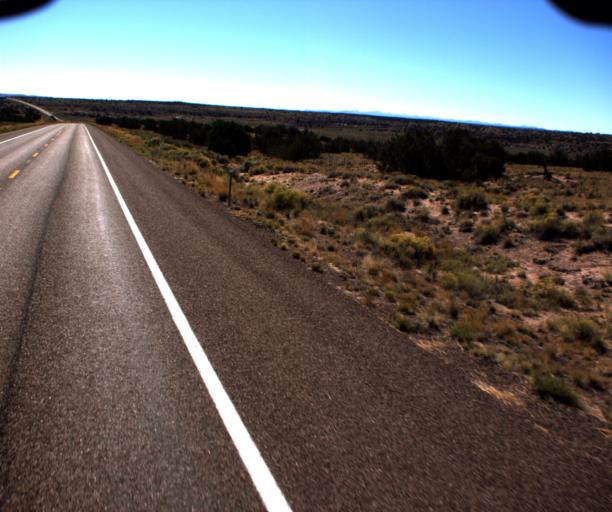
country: US
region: Arizona
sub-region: Apache County
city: Saint Johns
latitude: 34.6550
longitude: -109.7098
